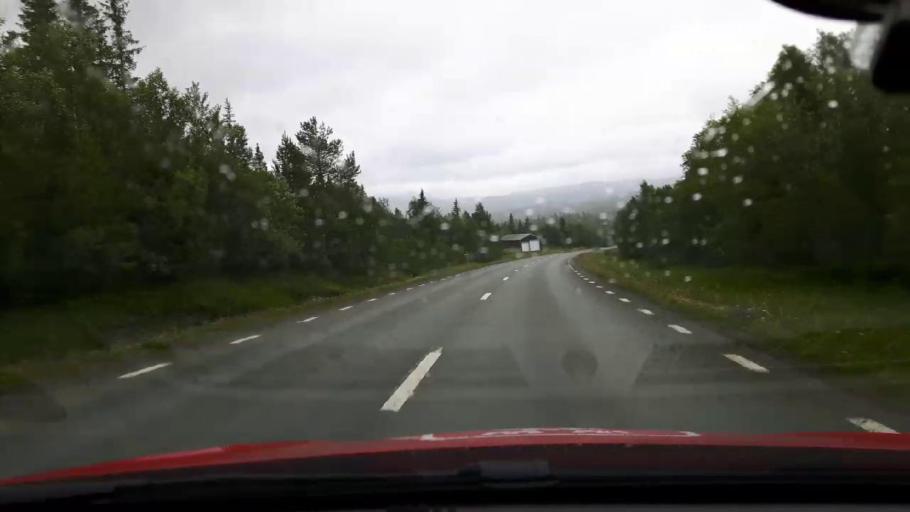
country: NO
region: Nord-Trondelag
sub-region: Meraker
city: Meraker
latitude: 63.2944
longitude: 12.1179
